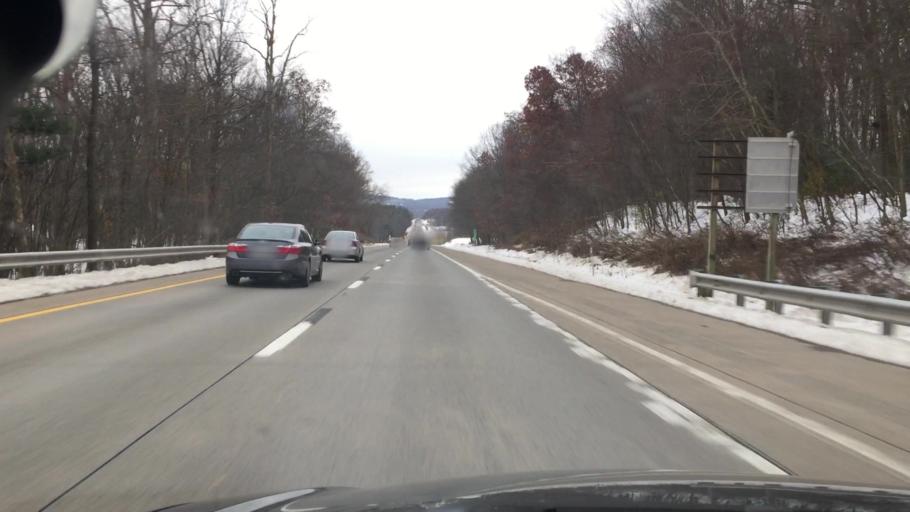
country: US
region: Pennsylvania
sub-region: Luzerne County
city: Nanticoke
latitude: 41.1399
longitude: -75.9636
